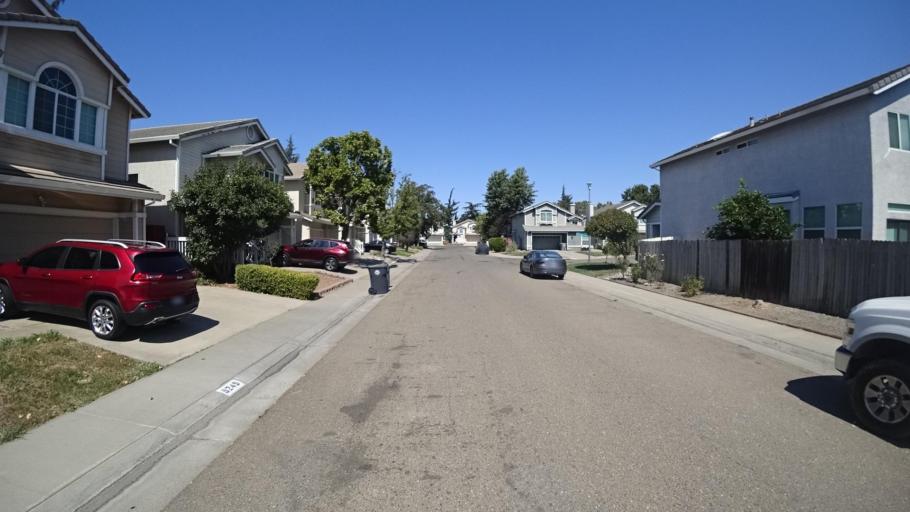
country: US
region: California
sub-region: Sacramento County
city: Laguna
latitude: 38.4220
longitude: -121.4139
